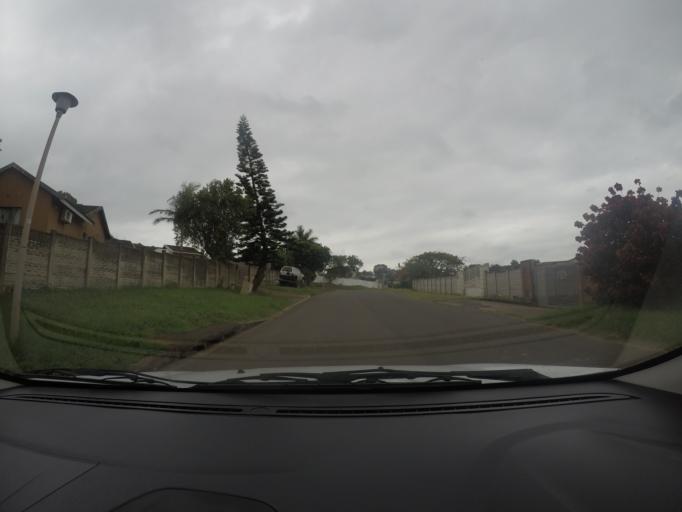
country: ZA
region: KwaZulu-Natal
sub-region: uThungulu District Municipality
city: Empangeni
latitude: -28.7622
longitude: 31.8829
